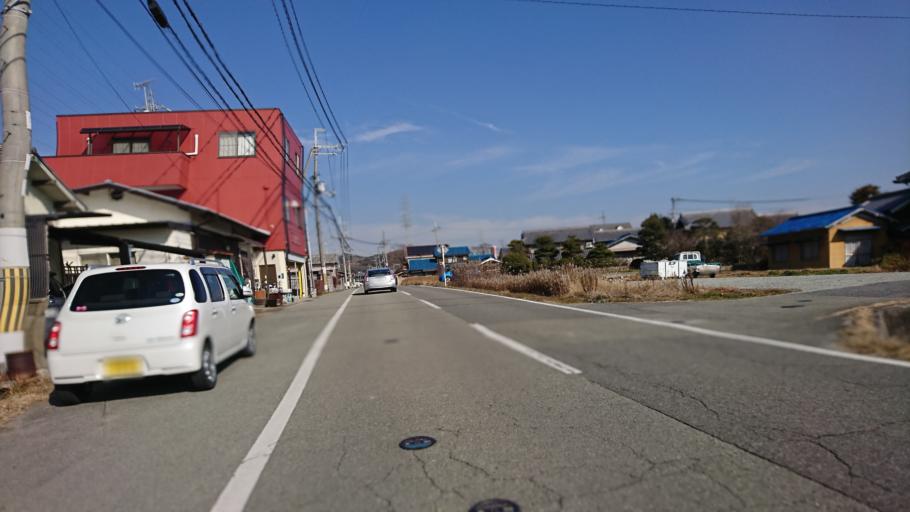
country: JP
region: Hyogo
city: Kakogawacho-honmachi
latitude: 34.8034
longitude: 134.8598
